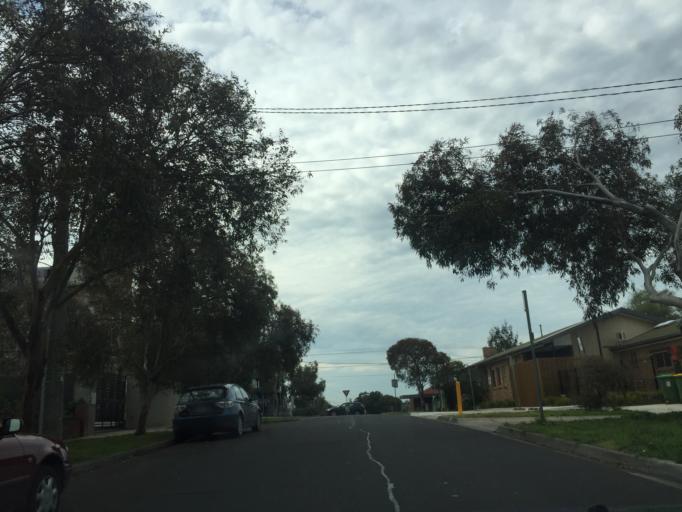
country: AU
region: Victoria
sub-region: Darebin
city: Thornbury
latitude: -37.7540
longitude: 145.0108
